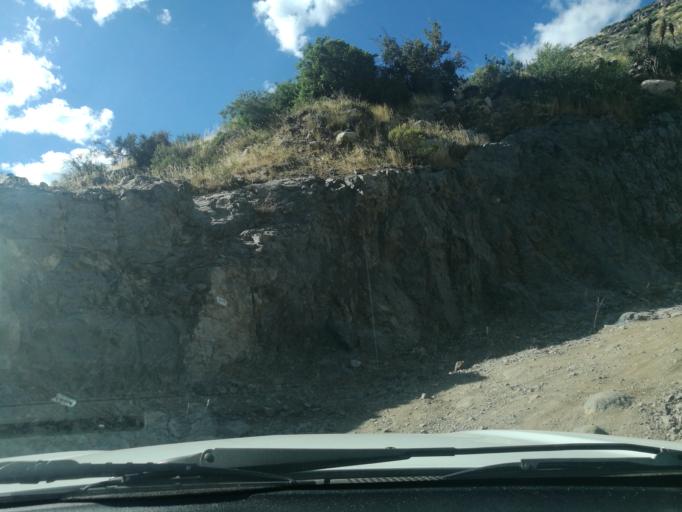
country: CL
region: O'Higgins
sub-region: Provincia de Cachapoal
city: Machali
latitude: -34.3633
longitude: -70.3045
